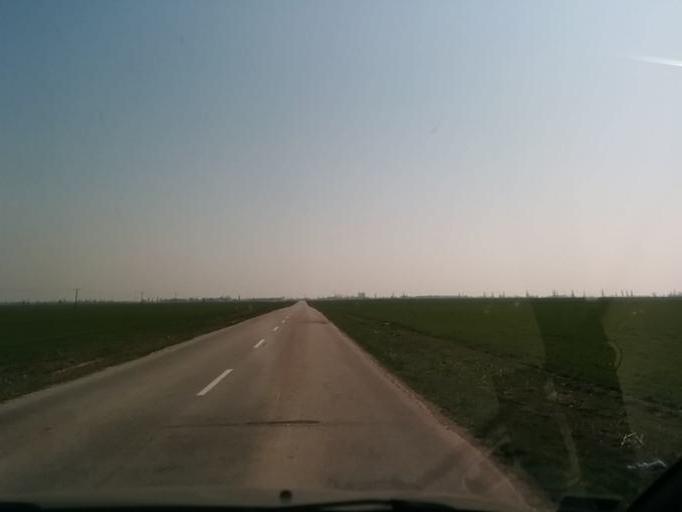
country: SK
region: Trnavsky
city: Sladkovicovo
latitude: 48.2140
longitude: 17.6033
